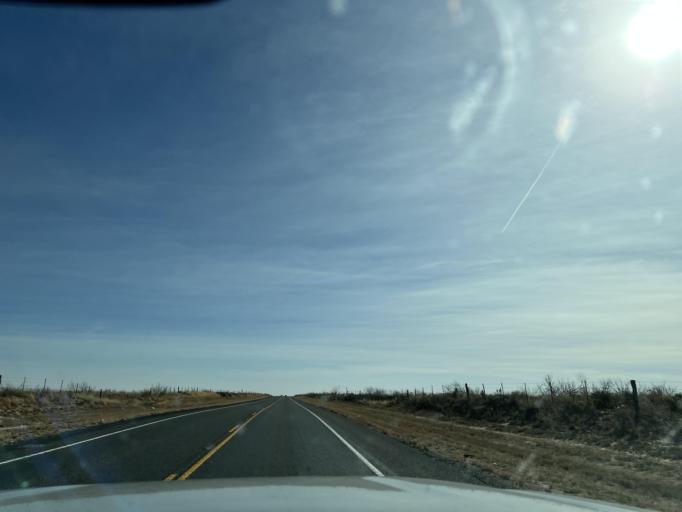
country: US
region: Texas
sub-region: Andrews County
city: Andrews
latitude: 32.4697
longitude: -102.4636
